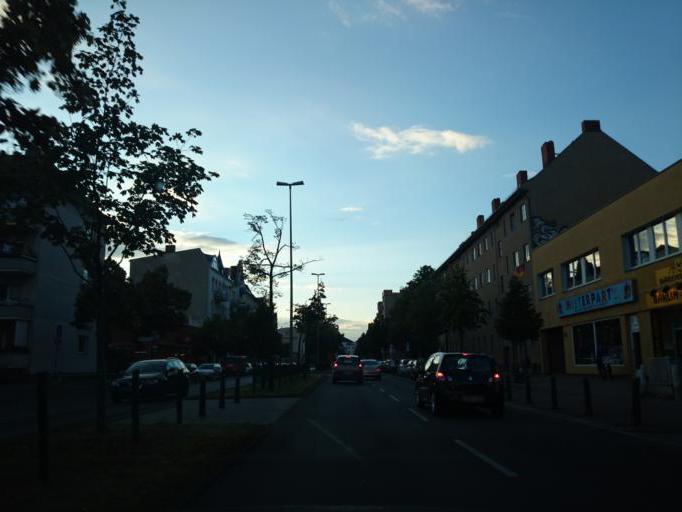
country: DE
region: Berlin
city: Wilhelmsruh
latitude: 52.5714
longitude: 13.3604
